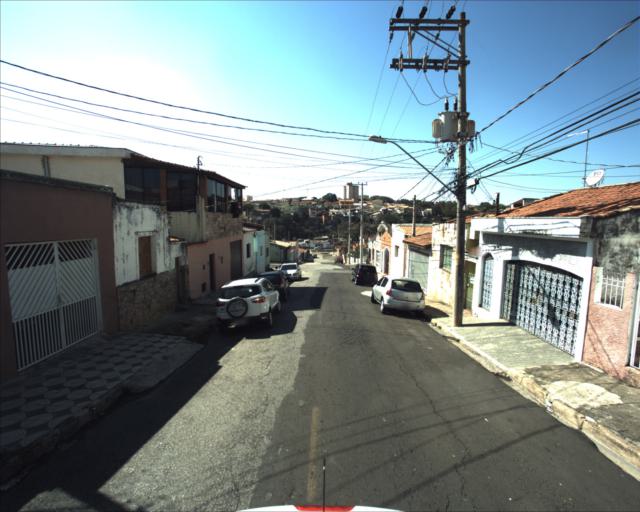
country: BR
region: Sao Paulo
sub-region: Sorocaba
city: Sorocaba
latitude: -23.5031
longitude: -47.4426
